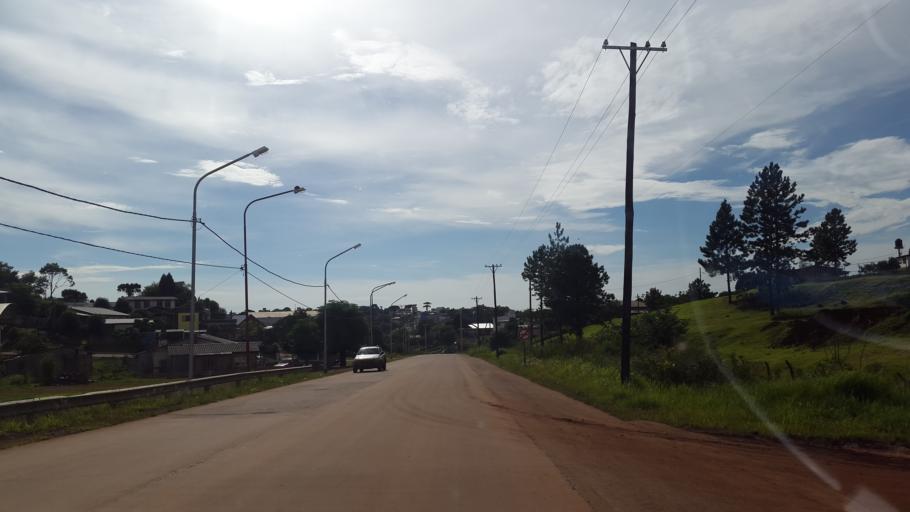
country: AR
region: Misiones
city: Bernardo de Irigoyen
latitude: -26.2602
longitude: -53.6469
